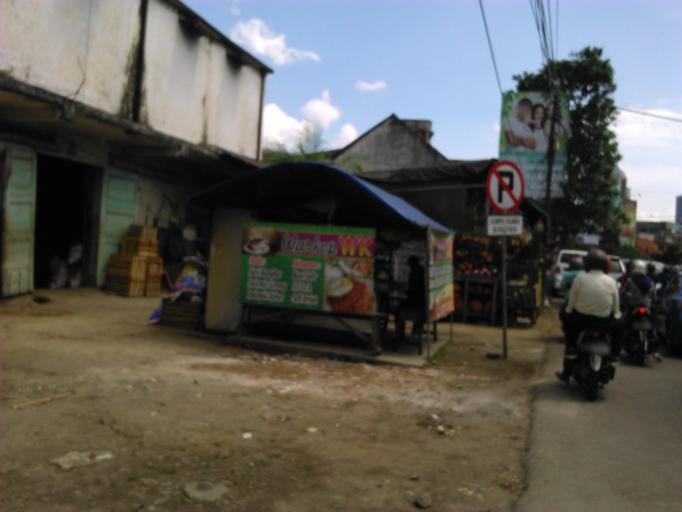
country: ID
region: East Java
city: Gubengairlangga
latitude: -7.2786
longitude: 112.7434
